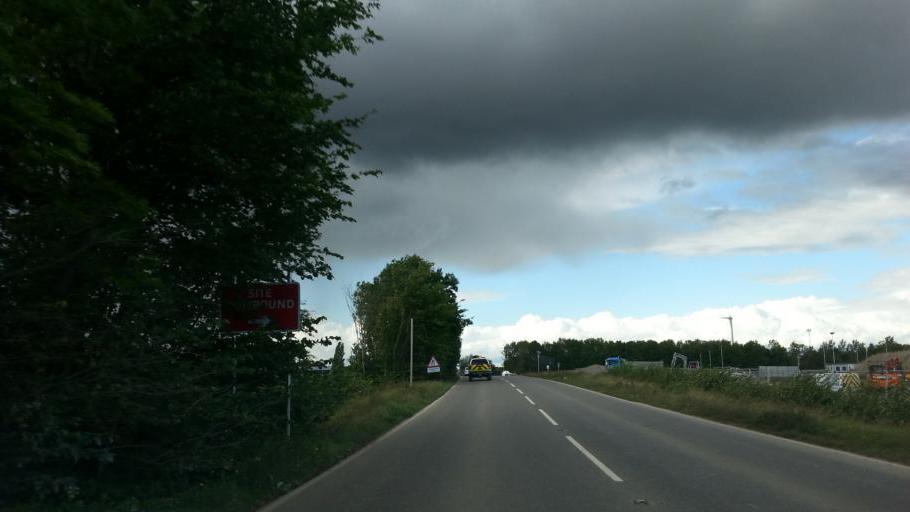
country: GB
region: England
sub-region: Cambridgeshire
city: Godmanchester
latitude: 52.2930
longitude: -0.1501
